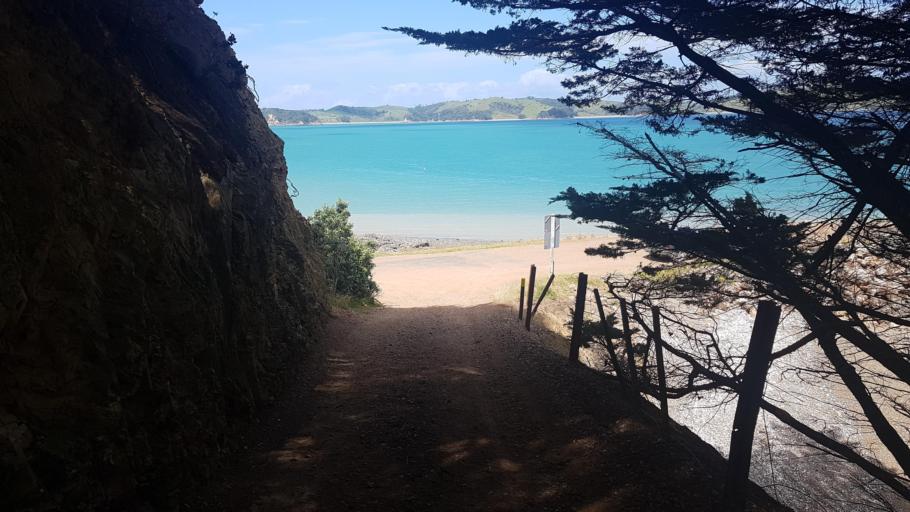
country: NZ
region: Auckland
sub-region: Auckland
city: Pakuranga
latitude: -36.8443
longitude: 175.1483
